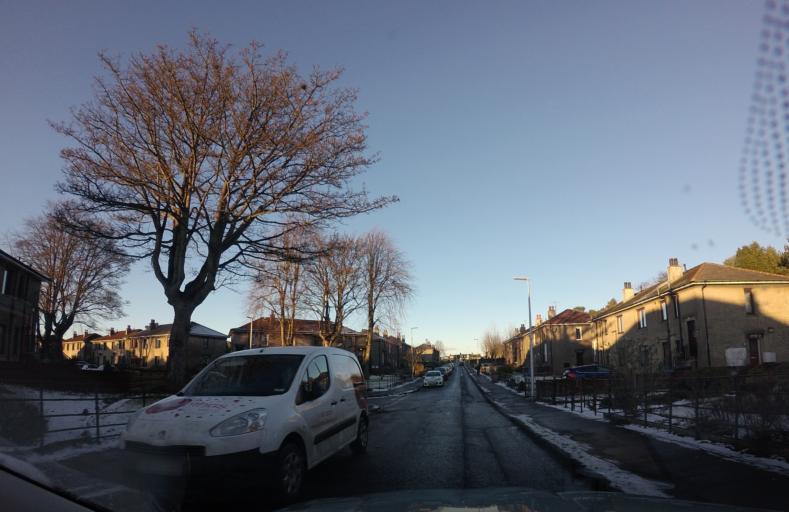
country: GB
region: Scotland
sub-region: Dundee City
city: Dundee
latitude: 56.4759
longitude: -2.9898
